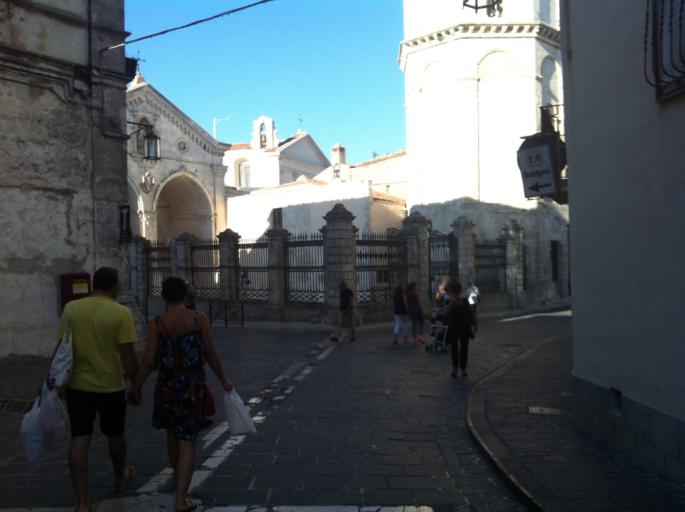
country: IT
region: Apulia
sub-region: Provincia di Foggia
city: Monte Sant'Angelo
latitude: 41.7077
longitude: 15.9543
